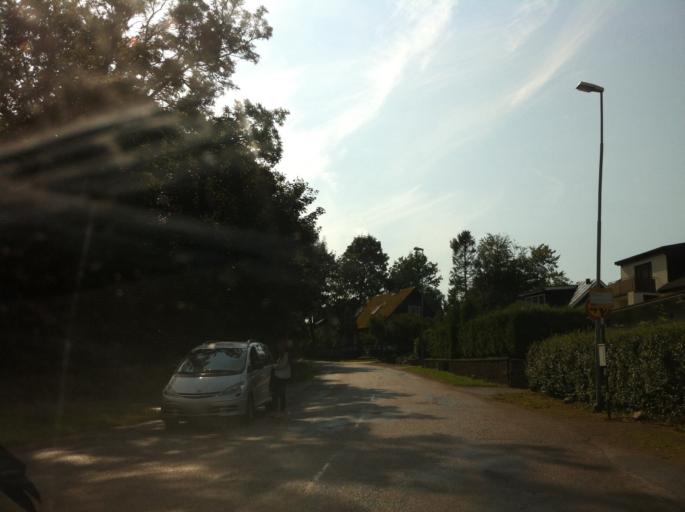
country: SE
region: Skane
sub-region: Helsingborg
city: Glumslov
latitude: 55.9311
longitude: 12.8744
